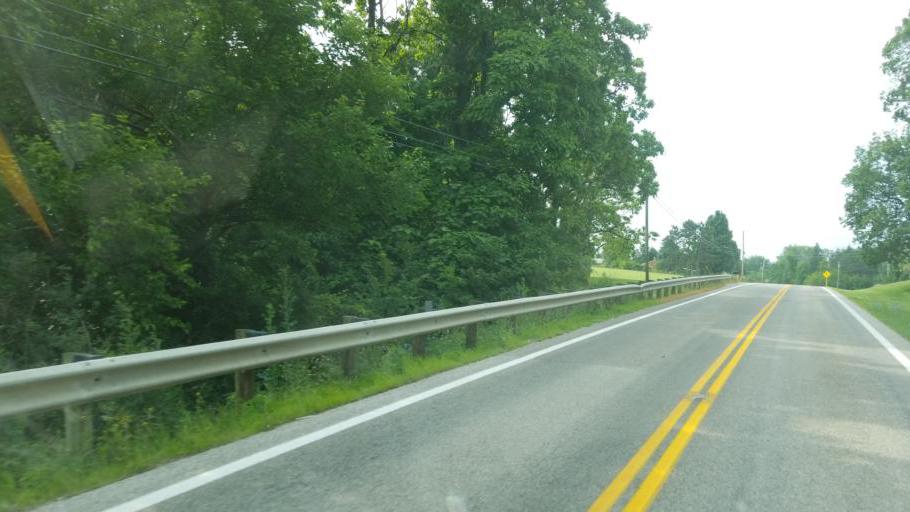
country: US
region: Ohio
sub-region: Knox County
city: Centerburg
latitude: 40.3527
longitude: -82.6909
